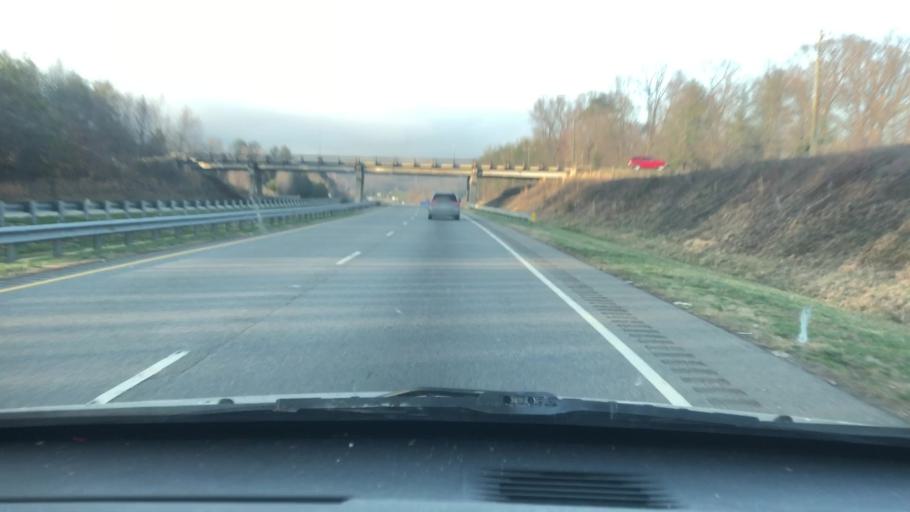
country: US
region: North Carolina
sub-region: Rockingham County
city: Mayodan
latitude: 36.4068
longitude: -79.9374
